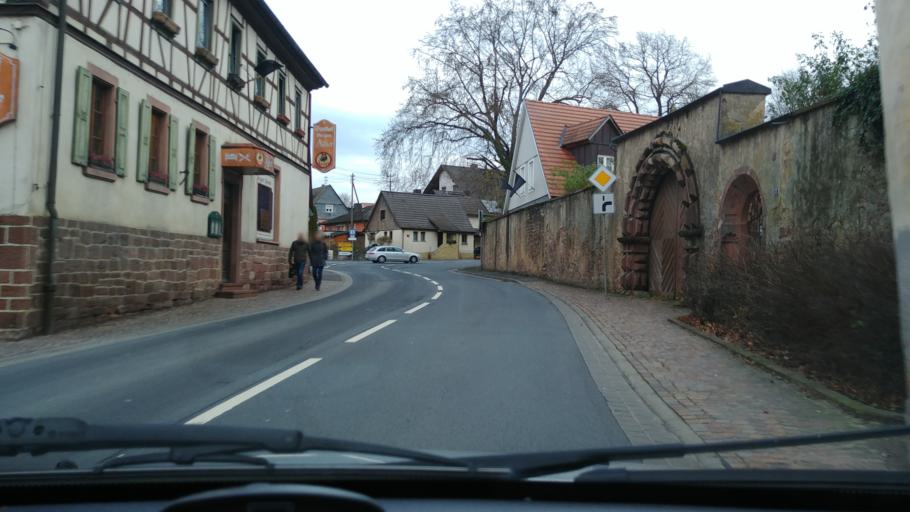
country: DE
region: Bavaria
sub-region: Regierungsbezirk Unterfranken
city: Lohr am Main
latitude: 50.0089
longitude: 9.6072
